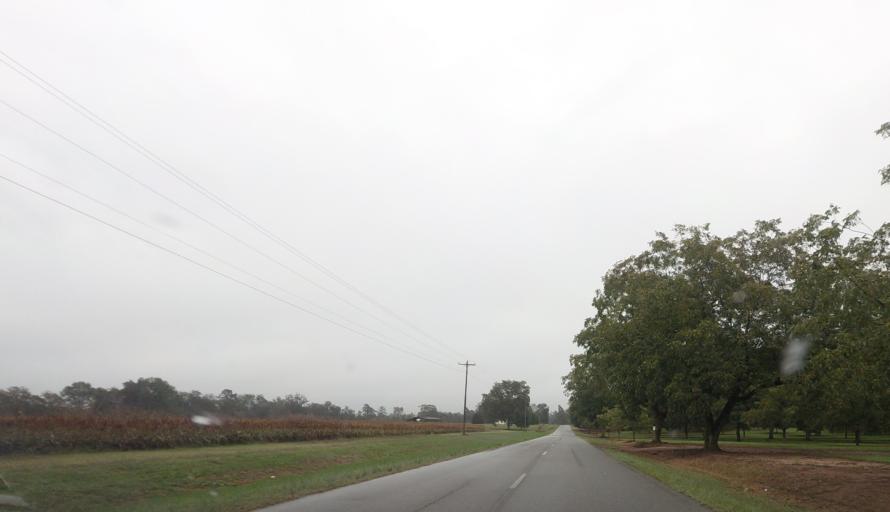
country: US
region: Georgia
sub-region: Peach County
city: Fort Valley
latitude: 32.5304
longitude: -83.9572
